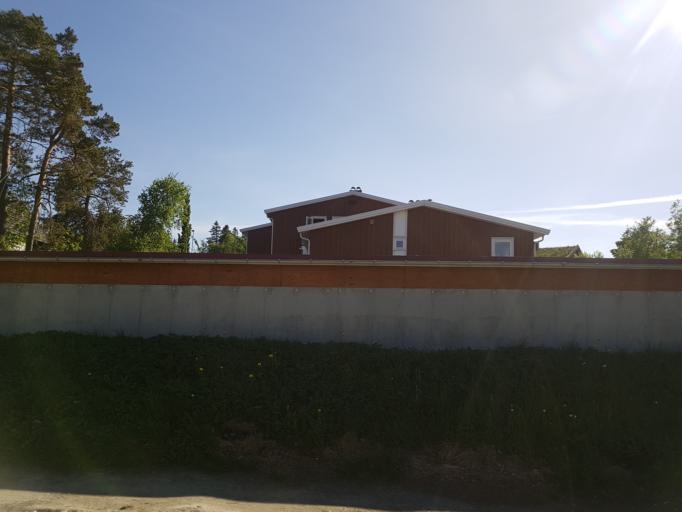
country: NO
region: Sor-Trondelag
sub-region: Trondheim
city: Trondheim
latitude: 63.4271
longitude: 10.5013
